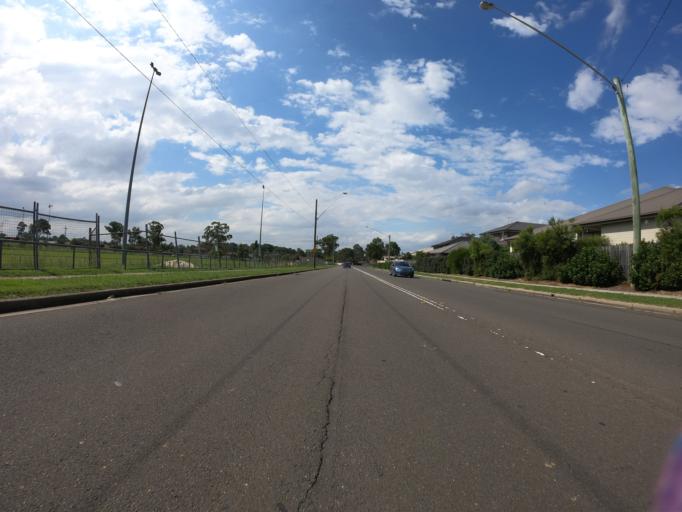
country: AU
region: New South Wales
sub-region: Blacktown
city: Blackett
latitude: -33.7453
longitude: 150.8281
